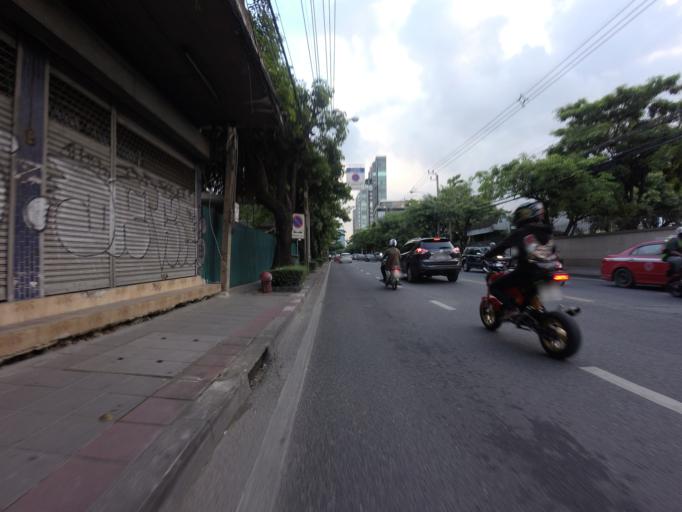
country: TH
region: Bangkok
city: Watthana
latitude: 13.7331
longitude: 100.5872
